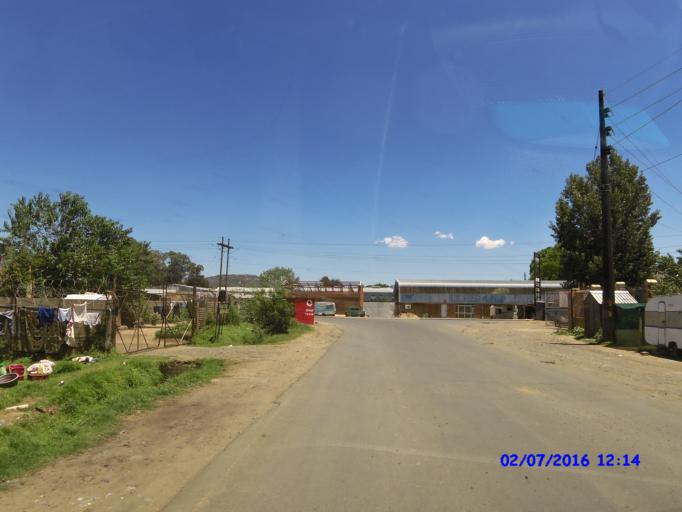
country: LS
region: Maseru
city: Maseru
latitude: -29.2963
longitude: 27.4737
